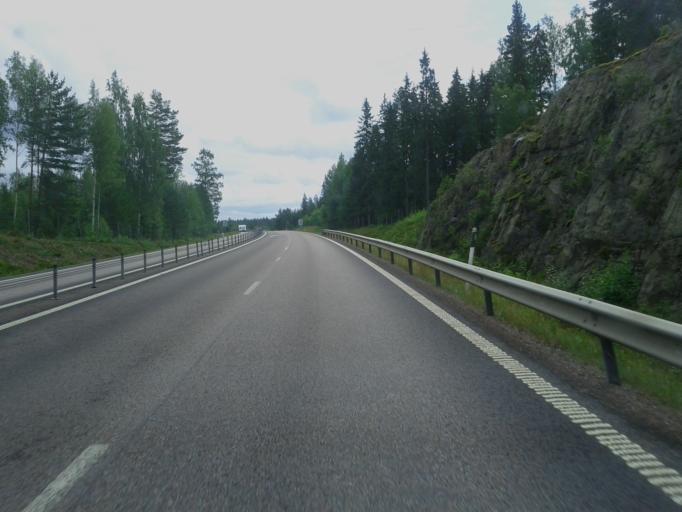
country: SE
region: Dalarna
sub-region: Saters Kommun
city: Saeter
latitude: 60.3619
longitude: 15.7195
